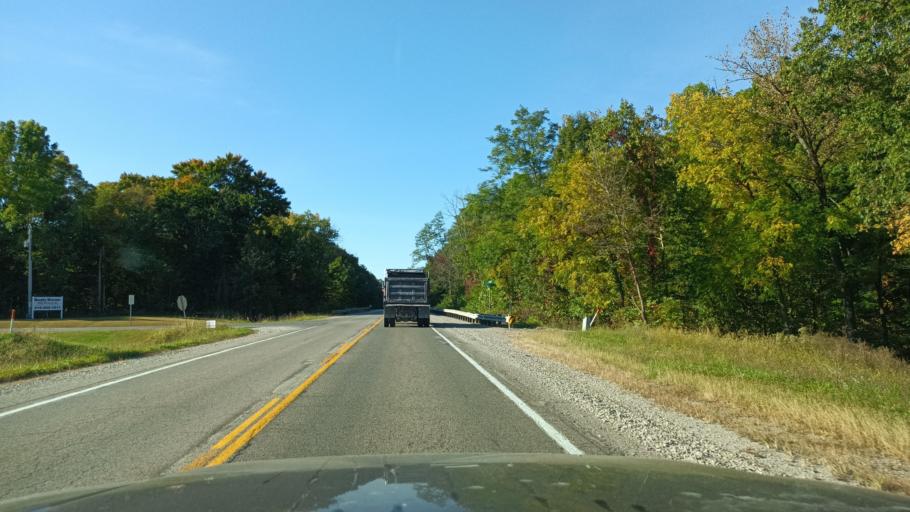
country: US
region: Illinois
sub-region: Clark County
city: Marshall
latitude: 39.4405
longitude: -87.6849
